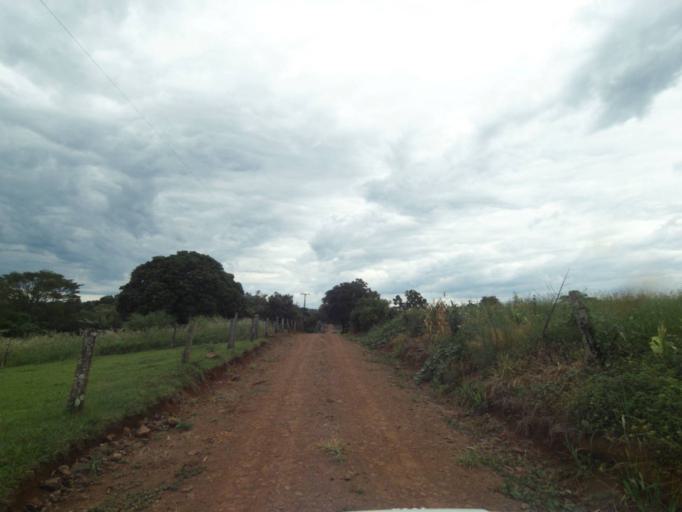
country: BR
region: Parana
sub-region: Guaraniacu
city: Guaraniacu
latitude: -24.9168
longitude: -52.9358
